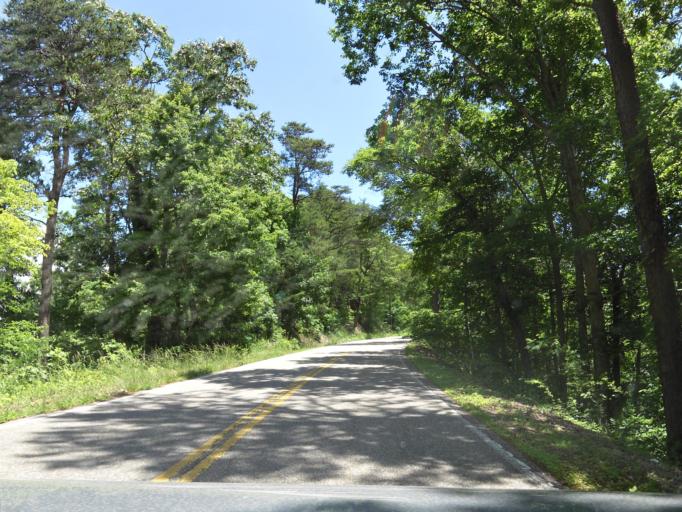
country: US
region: North Carolina
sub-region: Graham County
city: Robbinsville
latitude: 35.5041
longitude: -83.9749
